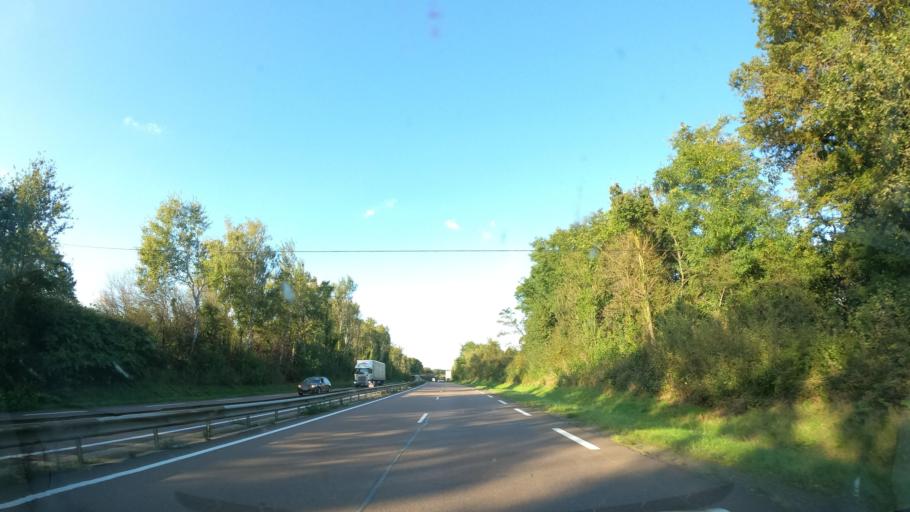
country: FR
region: Bourgogne
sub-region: Departement de Saone-et-Loire
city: Montceau-les-Mines
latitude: 46.6546
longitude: 4.3304
